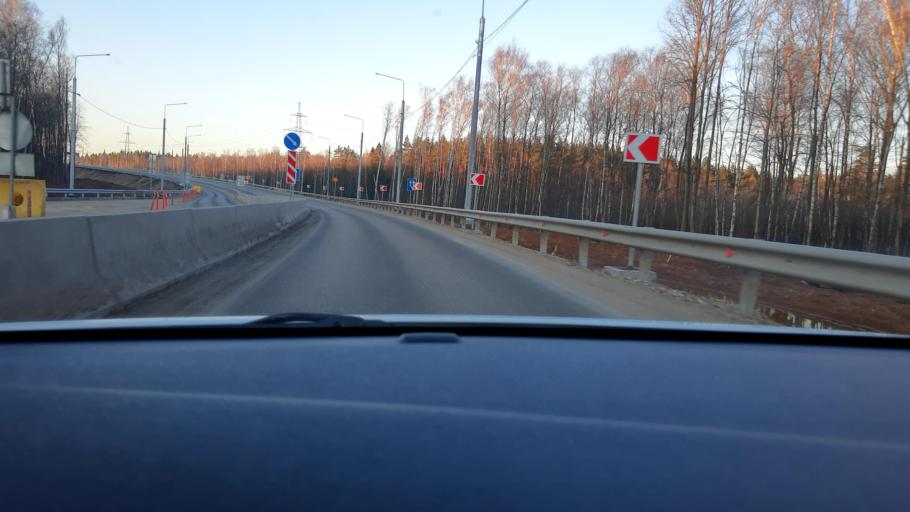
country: RU
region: Moskovskaya
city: Barvikha
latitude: 55.7182
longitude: 37.3130
